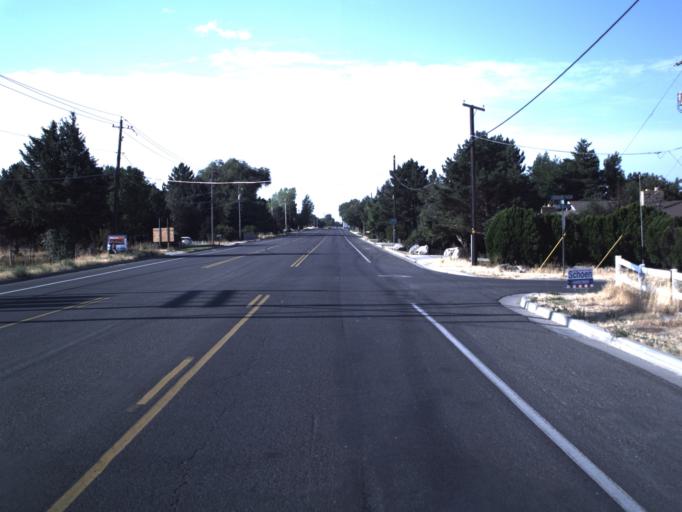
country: US
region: Utah
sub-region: Utah County
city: Alpine
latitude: 40.4418
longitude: -111.7843
